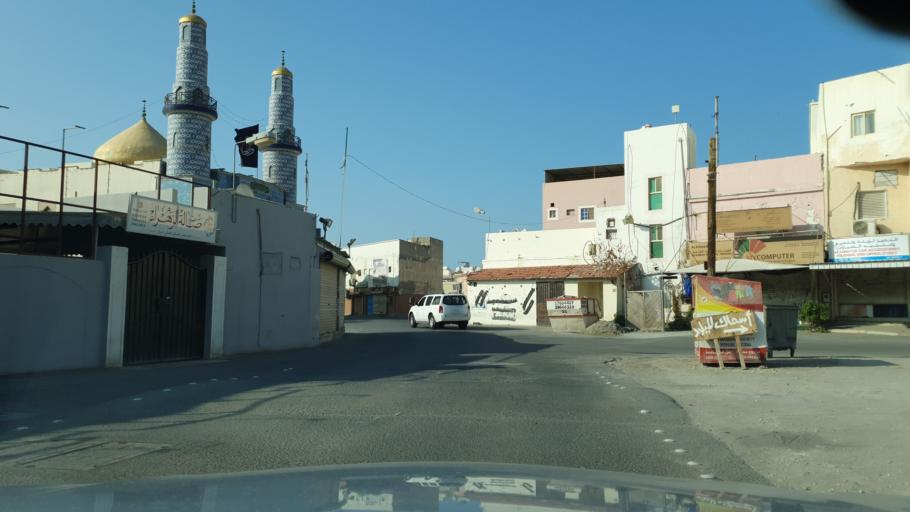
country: BH
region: Manama
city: Jidd Hafs
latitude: 26.2181
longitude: 50.4665
